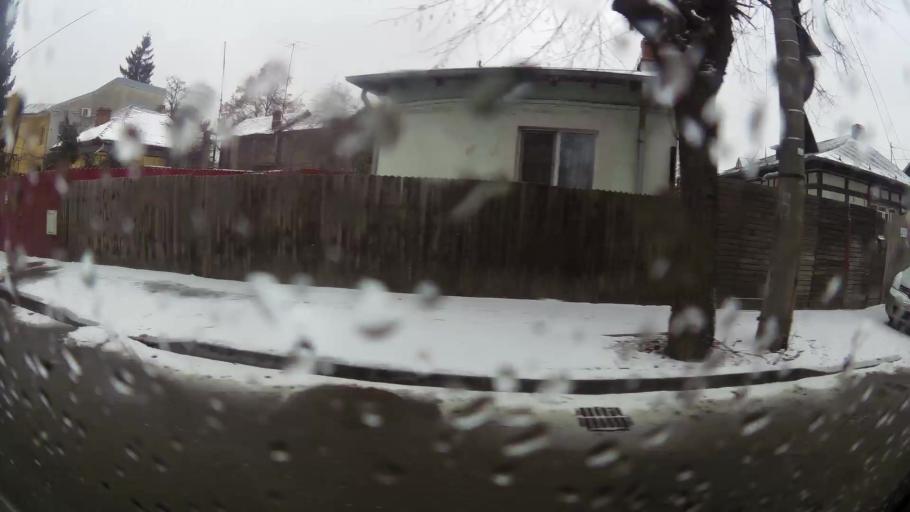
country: RO
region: Prahova
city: Ploiesti
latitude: 44.9408
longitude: 26.0083
